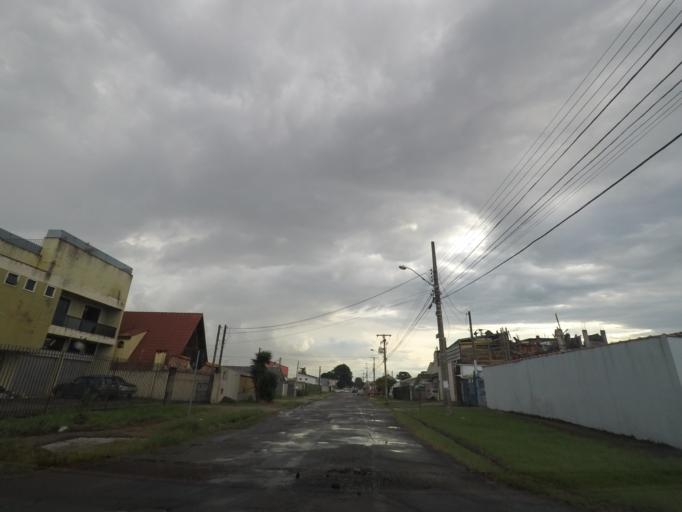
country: BR
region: Parana
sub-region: Curitiba
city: Curitiba
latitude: -25.4758
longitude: -49.2447
